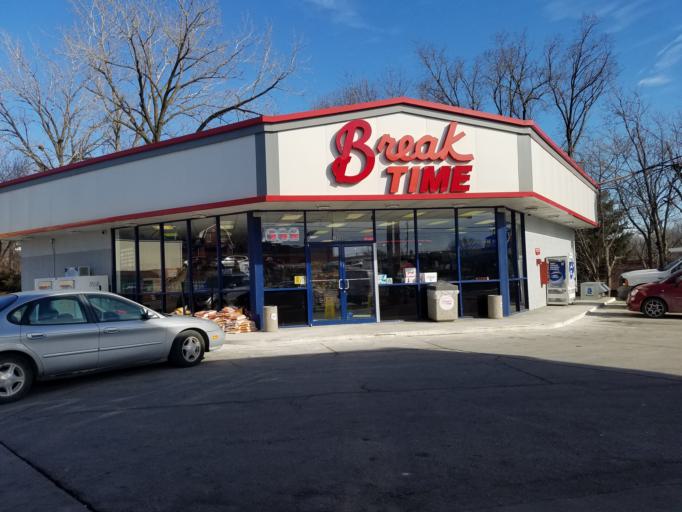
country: US
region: Missouri
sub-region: Cole County
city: Jefferson City
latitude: 38.5904
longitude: -92.2014
